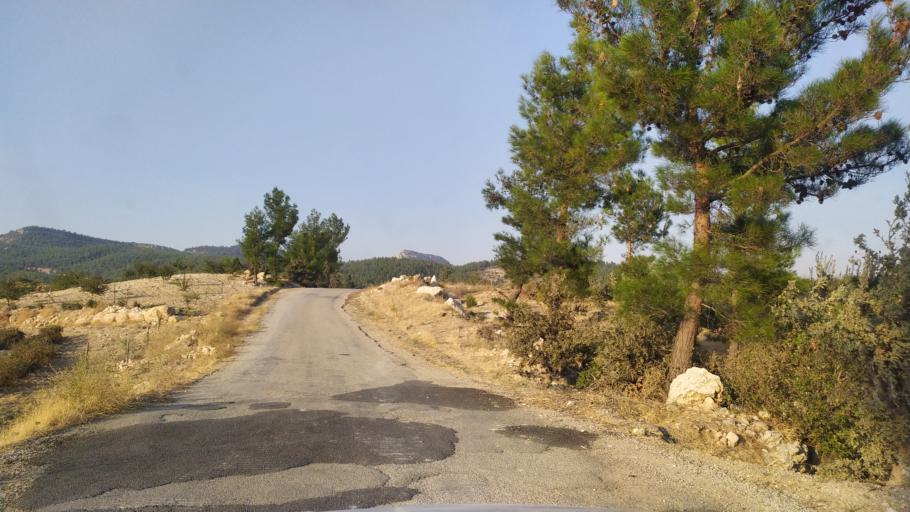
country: TR
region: Mersin
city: Mut
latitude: 36.6892
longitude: 33.1978
